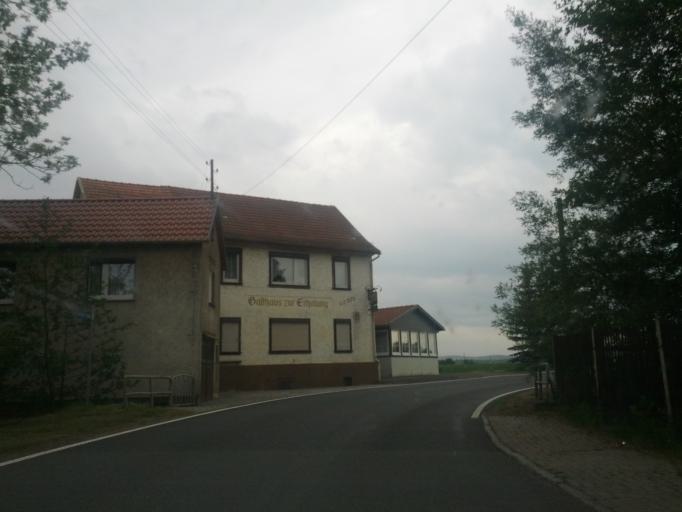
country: DE
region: Thuringia
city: Emleben
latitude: 50.8888
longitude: 10.6938
